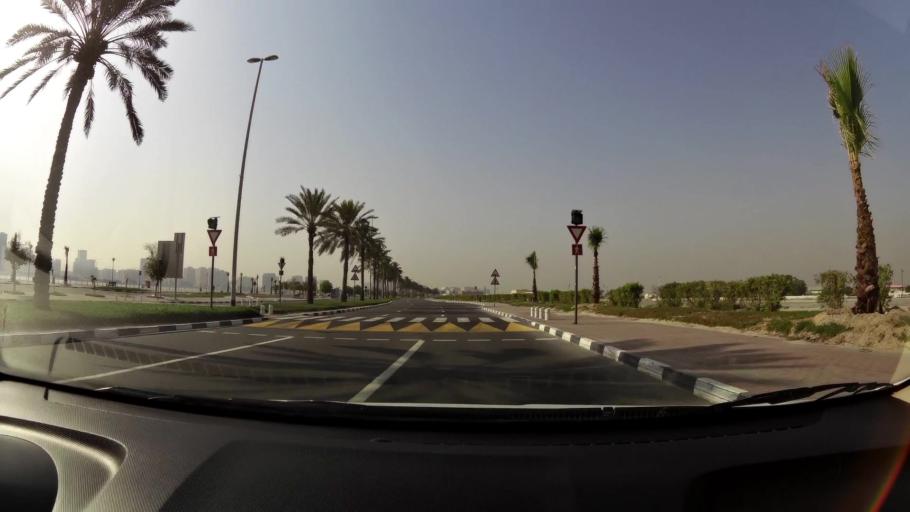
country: AE
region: Ash Shariqah
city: Sharjah
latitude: 25.3048
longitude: 55.3471
